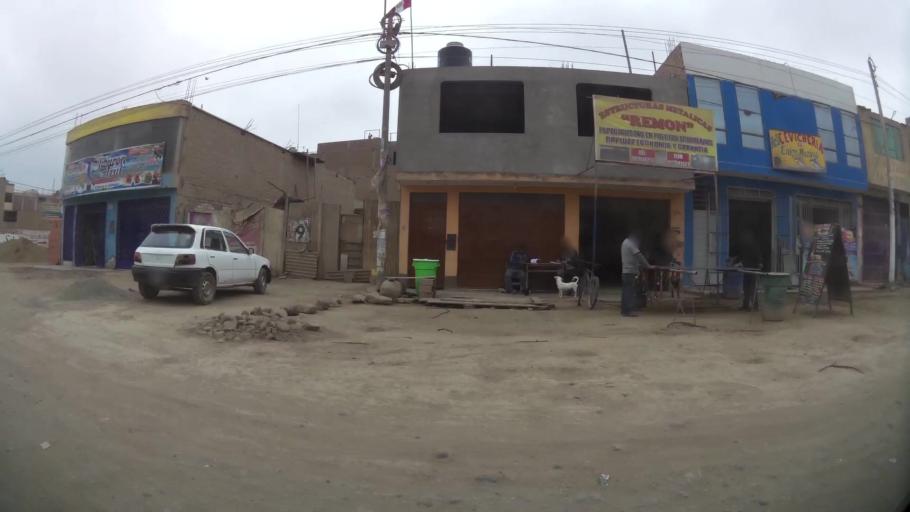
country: PE
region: Lima
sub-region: Lima
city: Independencia
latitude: -11.9602
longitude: -77.0959
